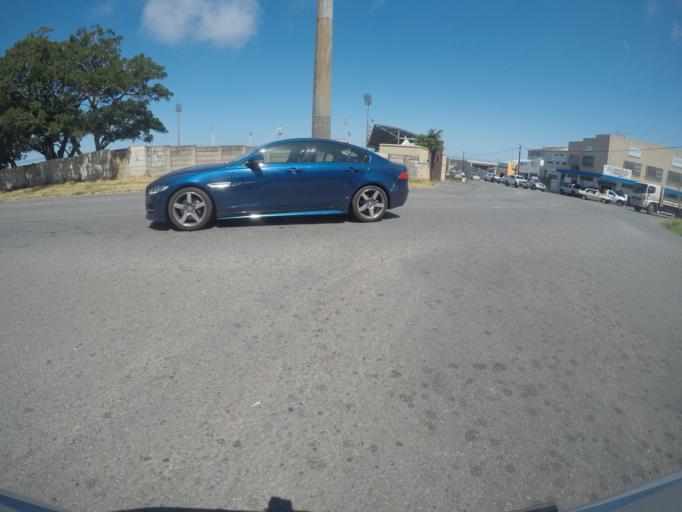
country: ZA
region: Eastern Cape
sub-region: Buffalo City Metropolitan Municipality
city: East London
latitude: -33.0063
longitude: 27.9042
